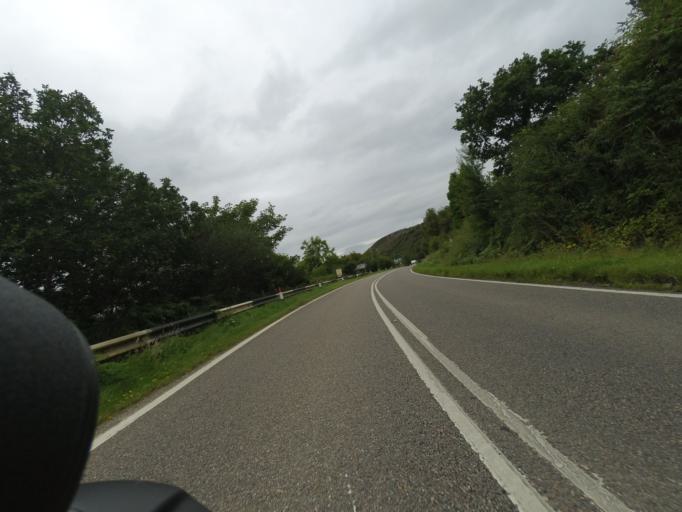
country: GB
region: Scotland
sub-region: Highland
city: Ullapool
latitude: 57.8916
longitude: -5.1413
